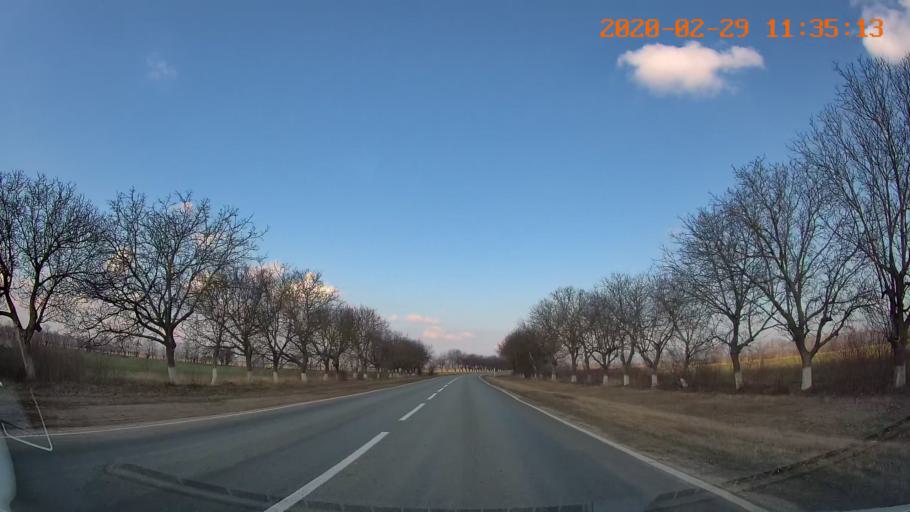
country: MD
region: Rezina
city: Saharna
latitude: 47.5770
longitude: 29.0653
